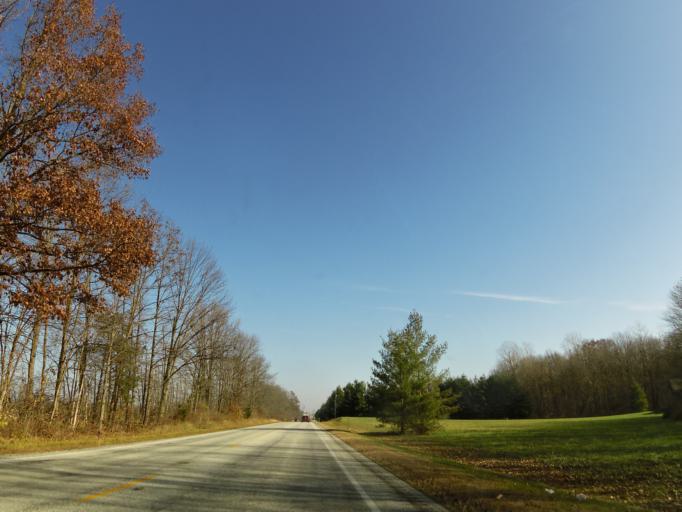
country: US
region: Indiana
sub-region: Shelby County
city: Shelbyville
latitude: 39.5494
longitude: -85.6817
